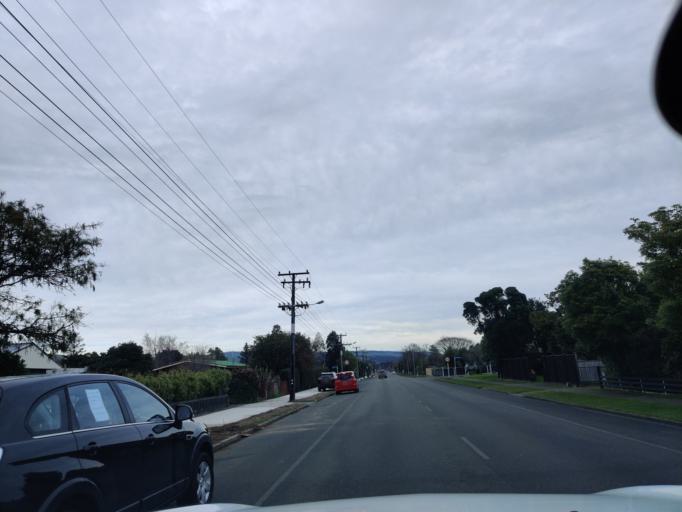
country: NZ
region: Manawatu-Wanganui
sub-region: Palmerston North City
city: Palmerston North
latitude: -40.2830
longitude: 175.7602
